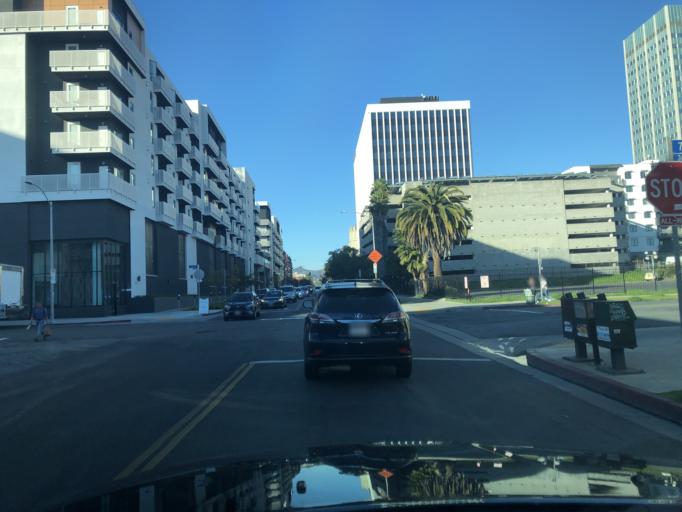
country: US
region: California
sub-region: Los Angeles County
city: Hollywood
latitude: 34.0595
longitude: -118.3053
